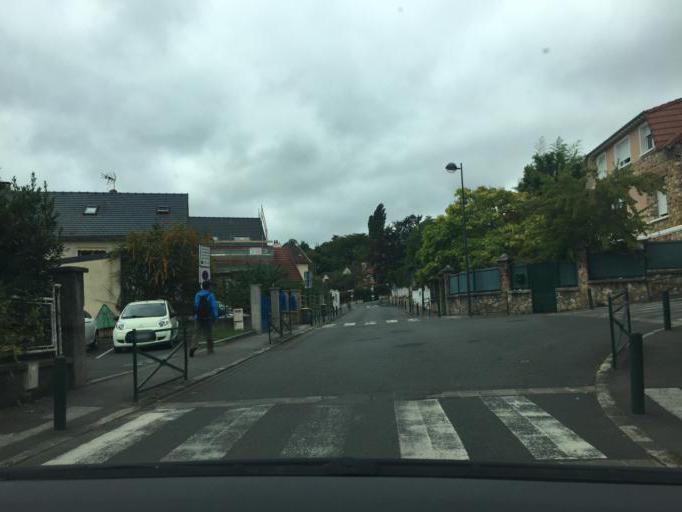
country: FR
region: Ile-de-France
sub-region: Departement de l'Essonne
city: Orsay
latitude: 48.7008
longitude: 2.1862
